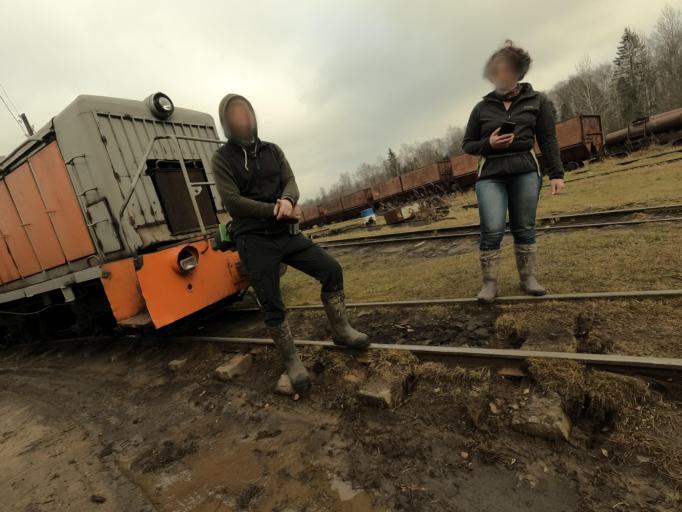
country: RU
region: Leningrad
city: Nurma
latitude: 59.5994
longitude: 31.2015
